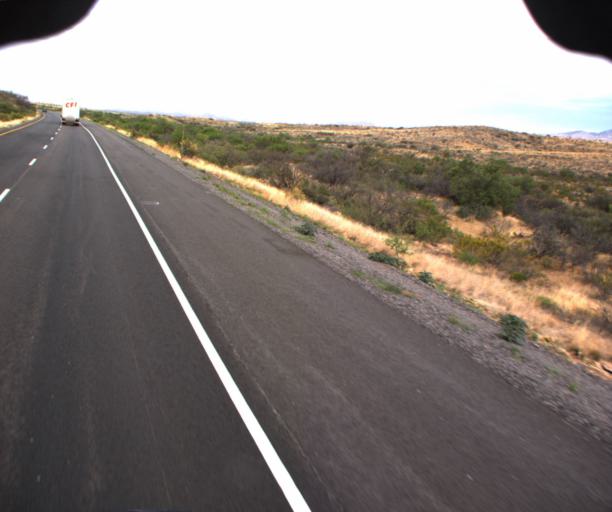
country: US
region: Arizona
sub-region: Cochise County
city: Mescal
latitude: 31.9706
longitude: -110.4754
